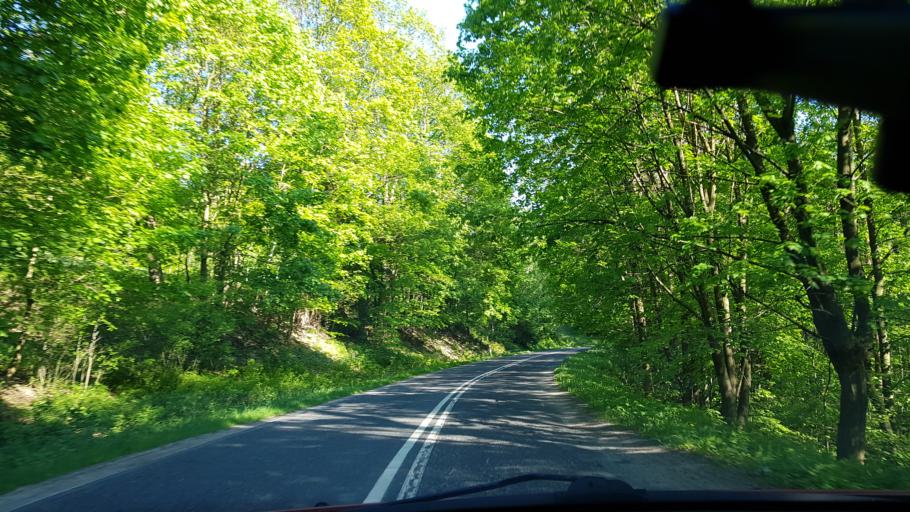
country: PL
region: Lower Silesian Voivodeship
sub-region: Powiat klodzki
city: Bozkow
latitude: 50.5775
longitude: 16.5982
